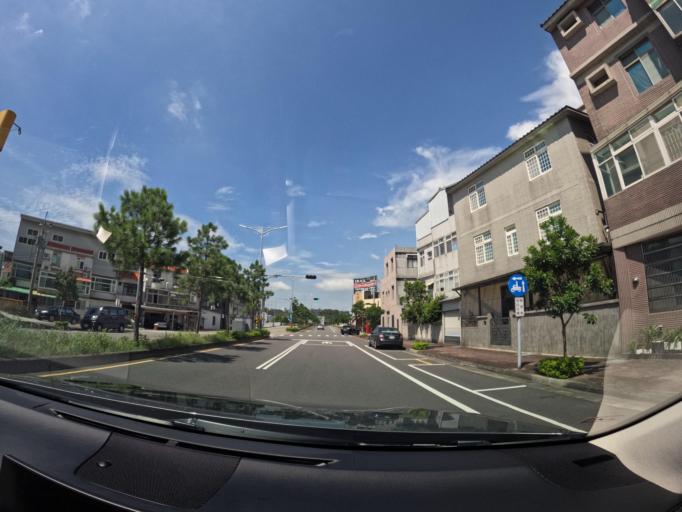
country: TW
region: Taiwan
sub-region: Hsinchu
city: Hsinchu
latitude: 24.6979
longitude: 120.9118
